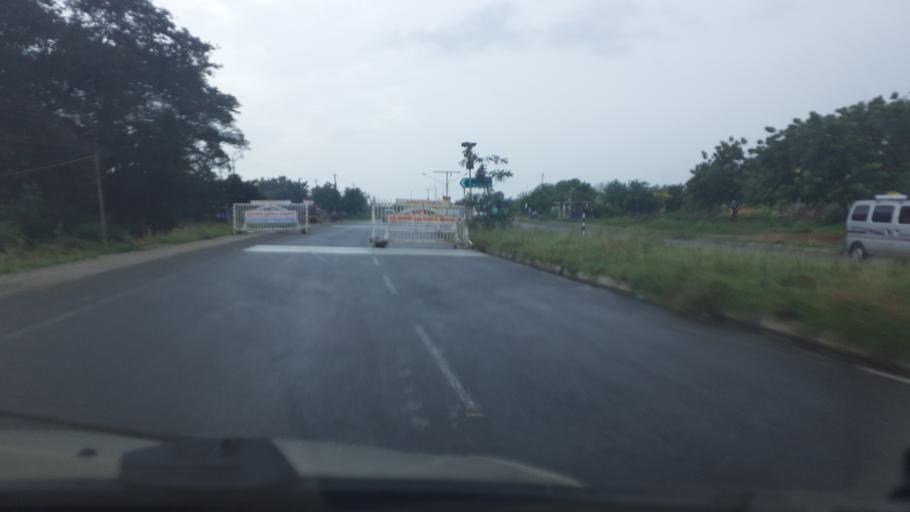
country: IN
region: Tamil Nadu
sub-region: Thoothukkudi
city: Kayattar
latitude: 9.0183
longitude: 77.7864
